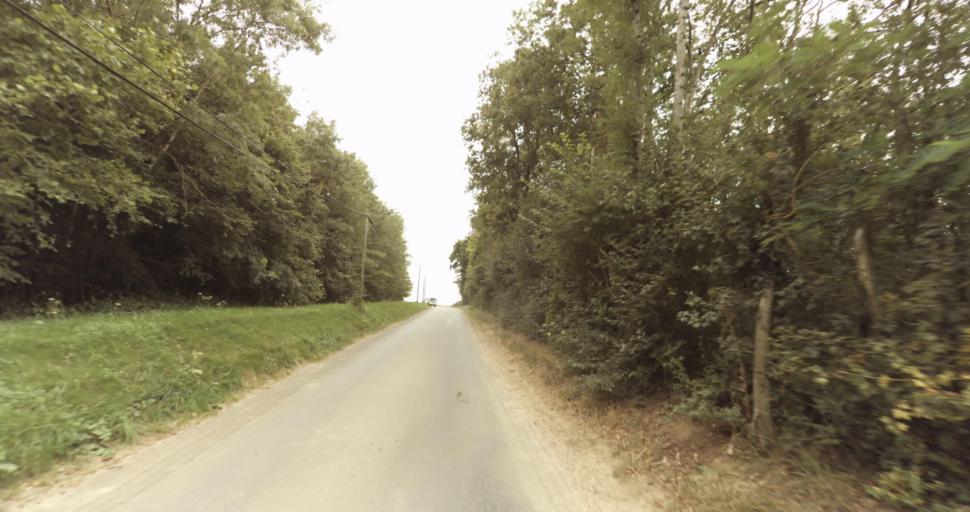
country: FR
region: Haute-Normandie
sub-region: Departement de l'Eure
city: Menilles
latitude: 49.0168
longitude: 1.3009
